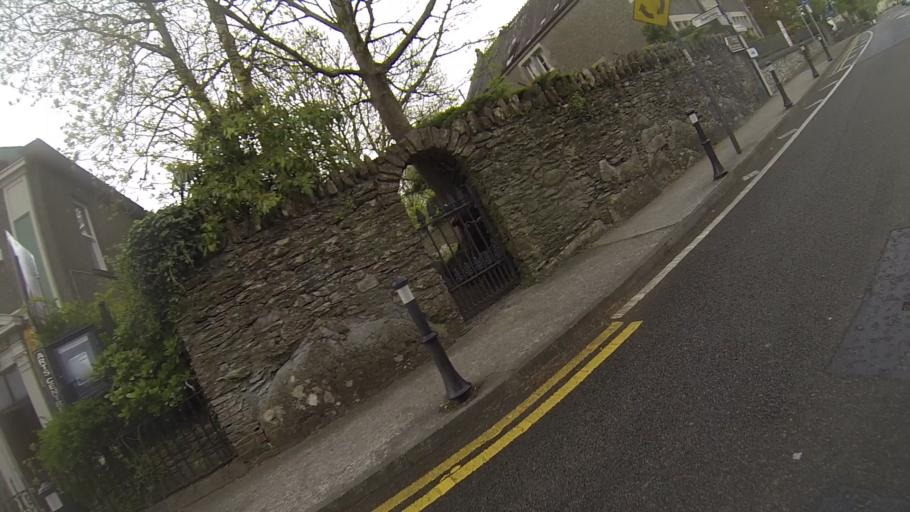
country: IE
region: Munster
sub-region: Ciarrai
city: Kenmare
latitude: 51.8791
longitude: -9.5809
